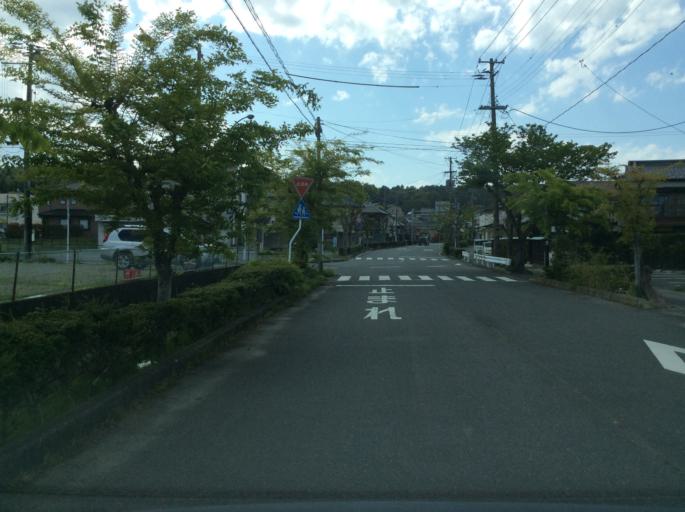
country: JP
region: Ibaraki
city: Kitaibaraki
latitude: 36.8832
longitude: 140.7861
